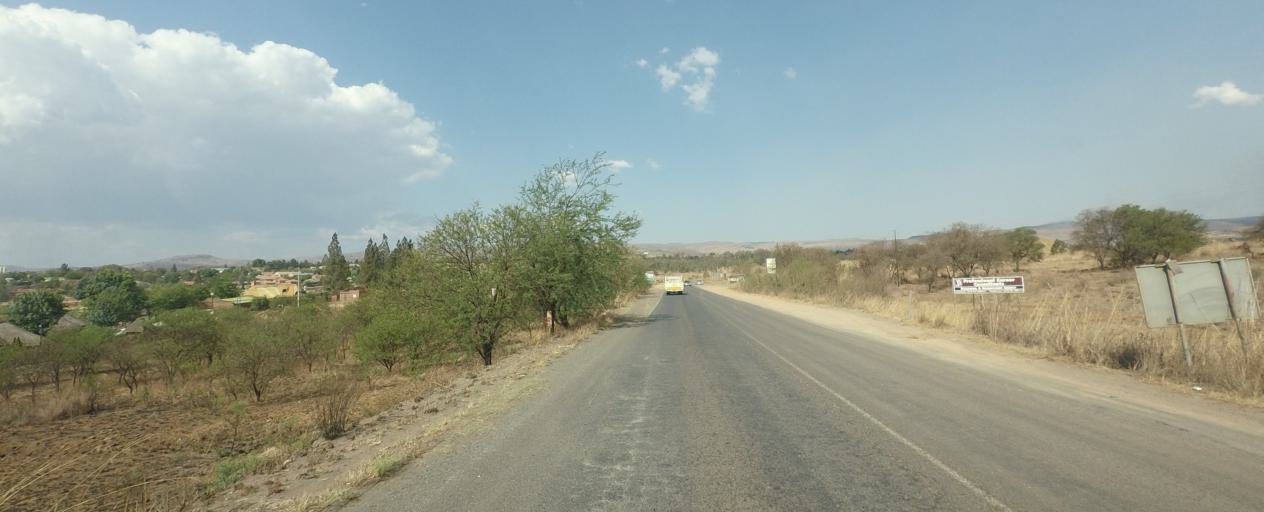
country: ZA
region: Mpumalanga
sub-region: Ehlanzeni District
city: Lydenburg
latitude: -25.1146
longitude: 30.4449
